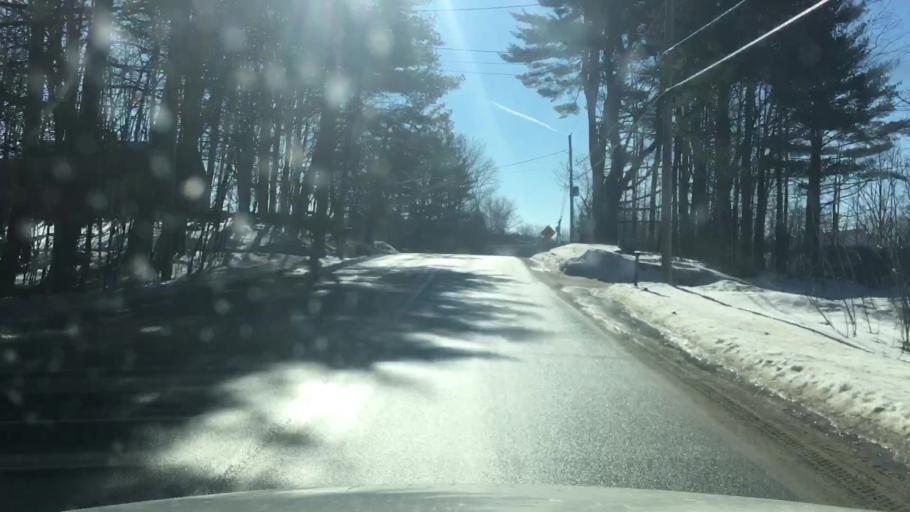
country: US
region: Maine
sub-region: Cumberland County
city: New Gloucester
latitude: 43.8723
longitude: -70.3334
